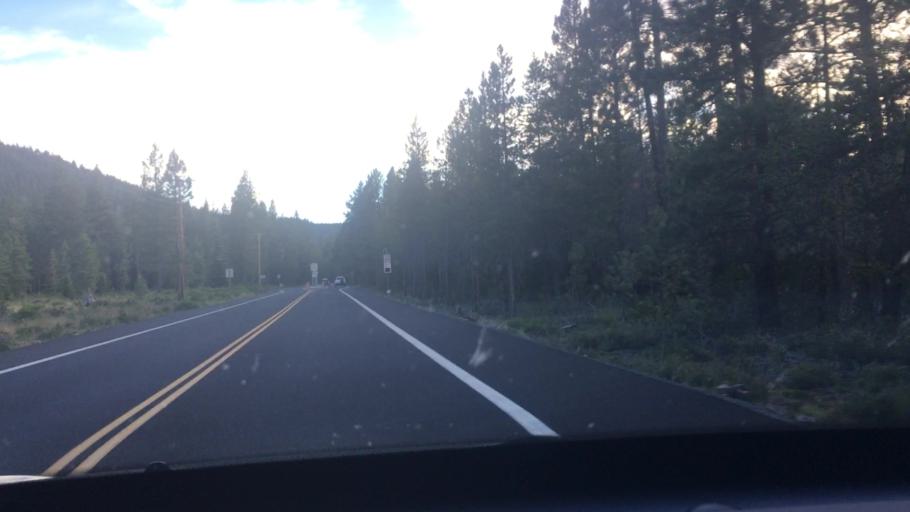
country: US
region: Oregon
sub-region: Deschutes County
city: Deschutes River Woods
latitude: 44.0372
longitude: -121.5037
